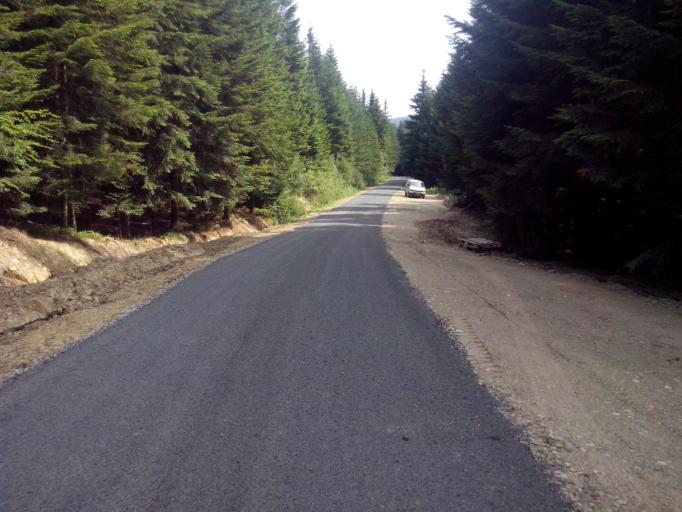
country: PL
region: Subcarpathian Voivodeship
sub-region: Powiat strzyzowski
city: Strzyzow
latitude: 49.8114
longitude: 21.8009
